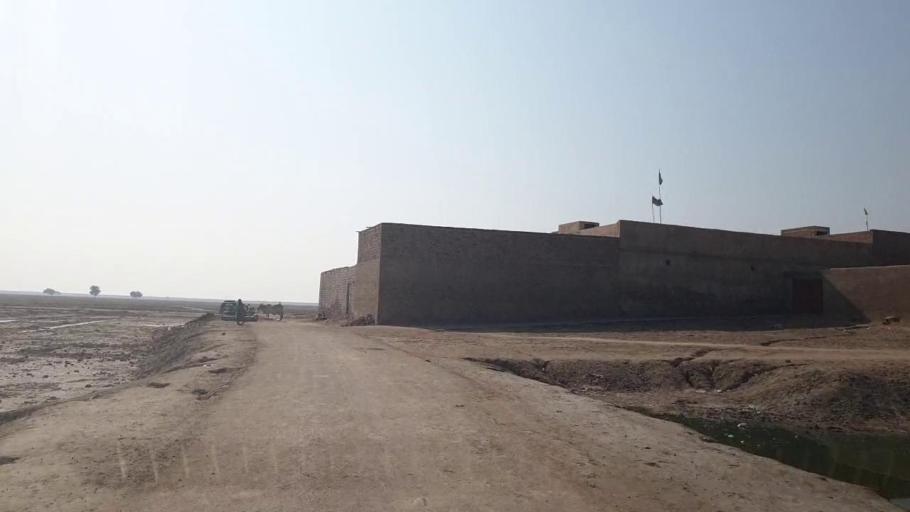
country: PK
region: Sindh
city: Bhan
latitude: 26.4345
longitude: 67.7350
